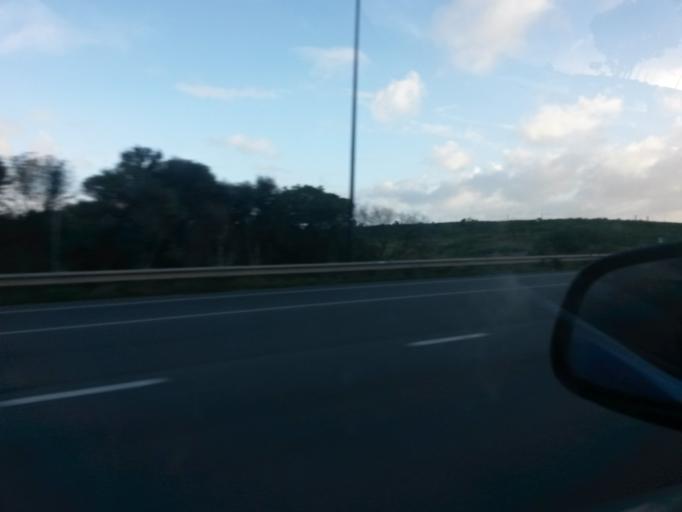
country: AU
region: South Australia
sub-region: Port Adelaide Enfield
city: Blair Athol
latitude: -34.8327
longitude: 138.5683
